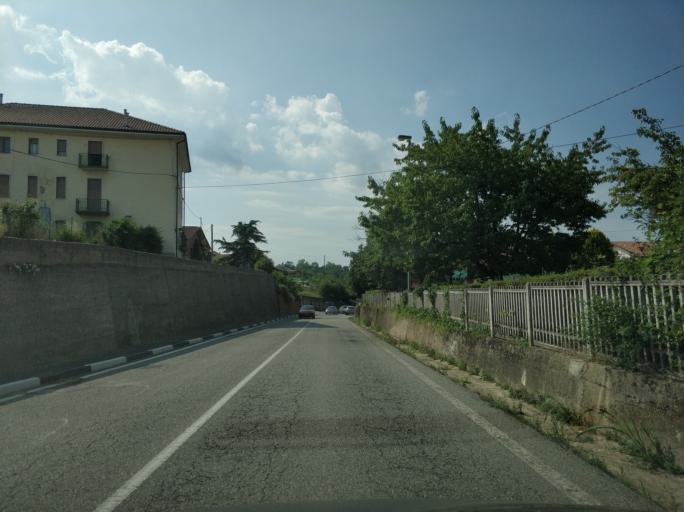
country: IT
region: Piedmont
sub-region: Provincia di Torino
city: Pralormo
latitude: 44.8695
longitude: 7.8958
